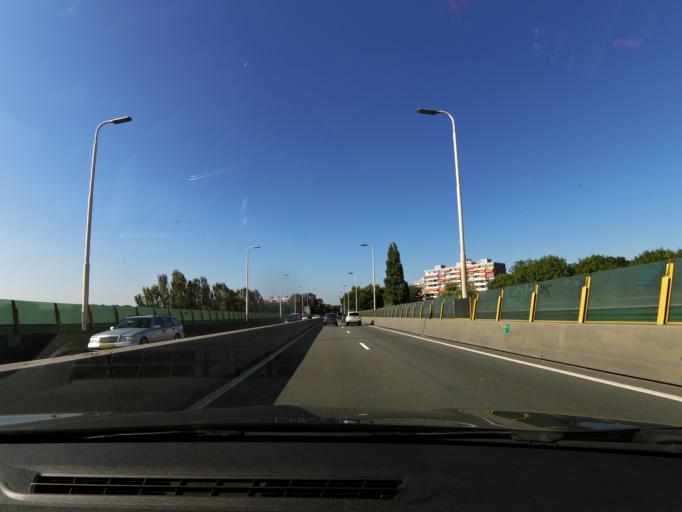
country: NL
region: South Holland
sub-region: Gemeente Papendrecht
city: Papendrecht
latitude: 51.8256
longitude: 4.7055
